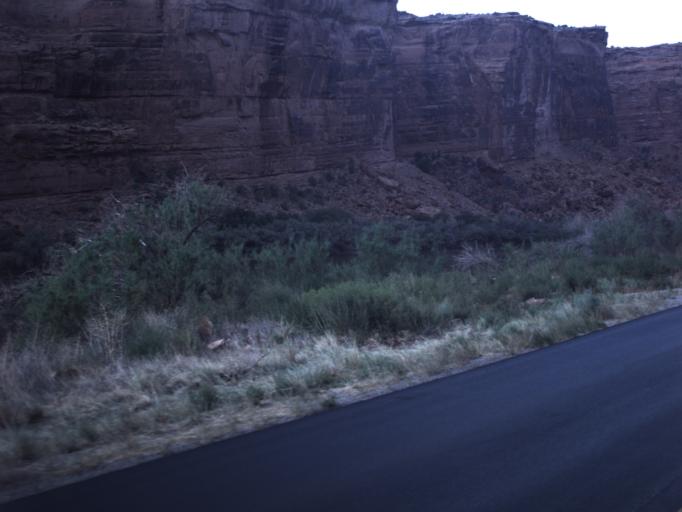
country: US
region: Utah
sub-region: Grand County
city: Moab
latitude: 38.6209
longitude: -109.5188
